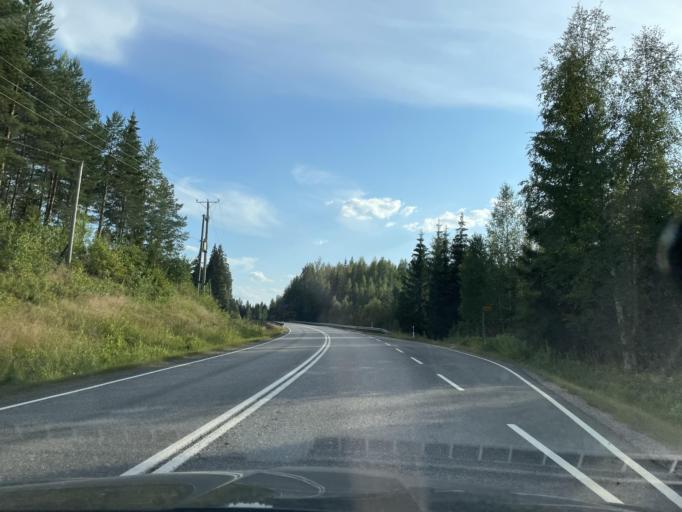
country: FI
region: Paijanne Tavastia
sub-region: Lahti
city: Auttoinen
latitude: 61.3169
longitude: 25.1312
